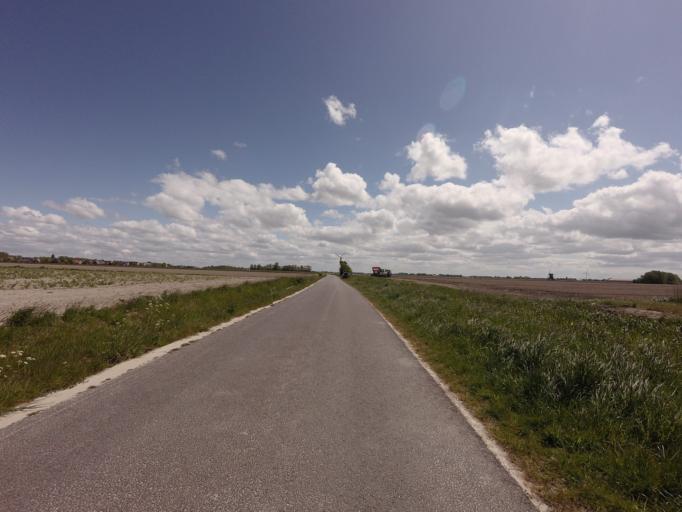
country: NL
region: Friesland
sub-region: Gemeente Harlingen
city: Harlingen
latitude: 53.1388
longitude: 5.4239
